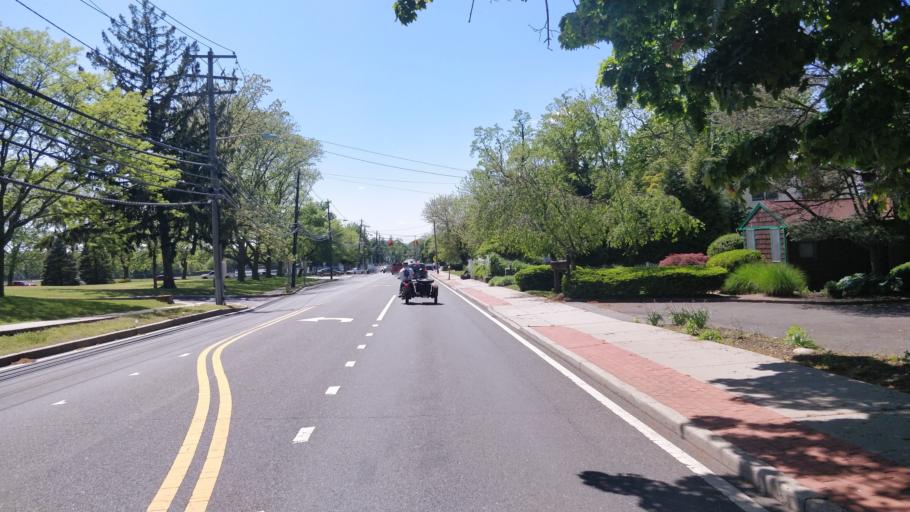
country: US
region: New York
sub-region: Suffolk County
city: Hauppauge
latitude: 40.8258
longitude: -73.1983
